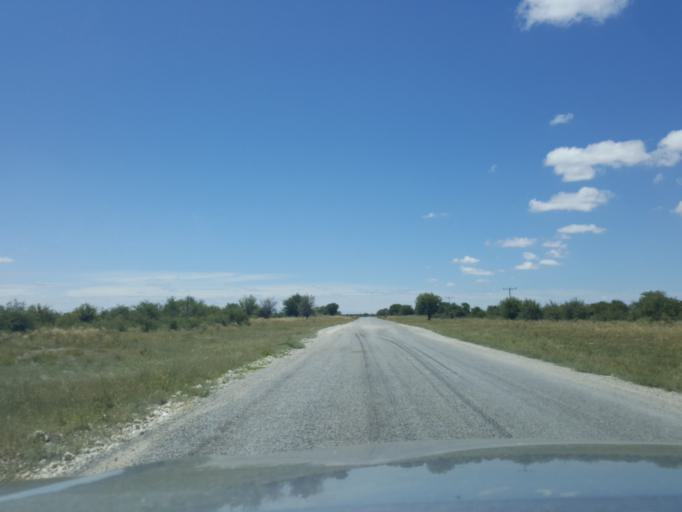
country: BW
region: Central
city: Nata
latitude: -20.1563
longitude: 25.8318
